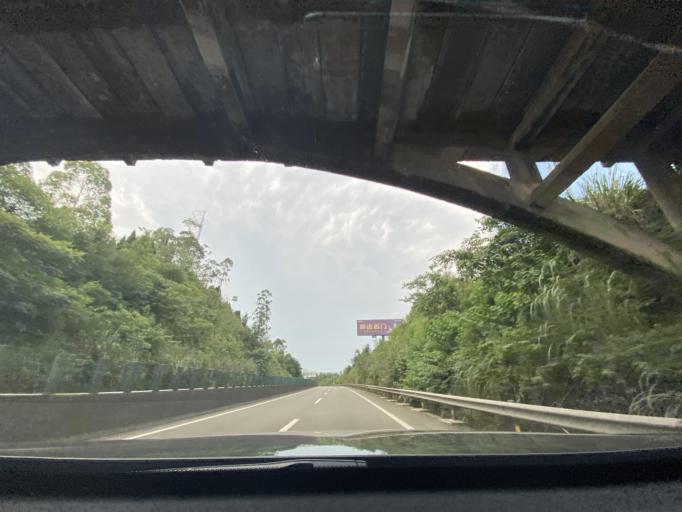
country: CN
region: Sichuan
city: Neijiang
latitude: 29.6453
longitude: 104.9854
